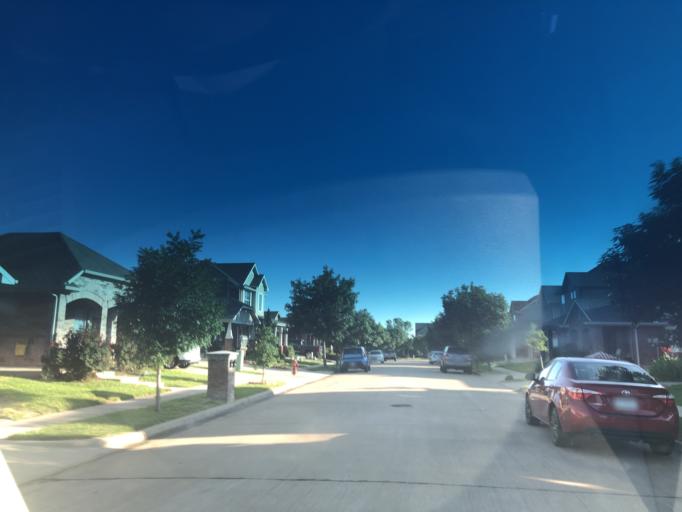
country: US
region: Texas
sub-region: Dallas County
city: Grand Prairie
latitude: 32.7068
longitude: -97.0185
